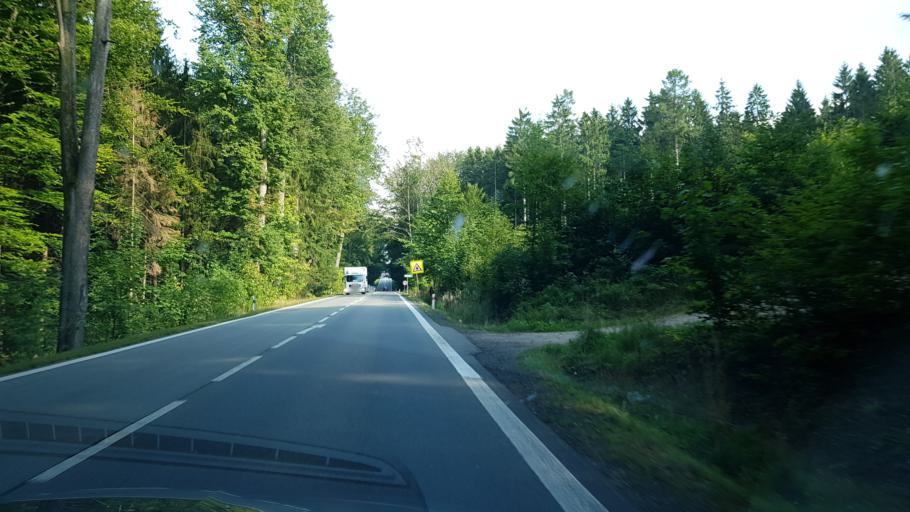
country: CZ
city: Vamberk
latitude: 50.1180
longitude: 16.3511
